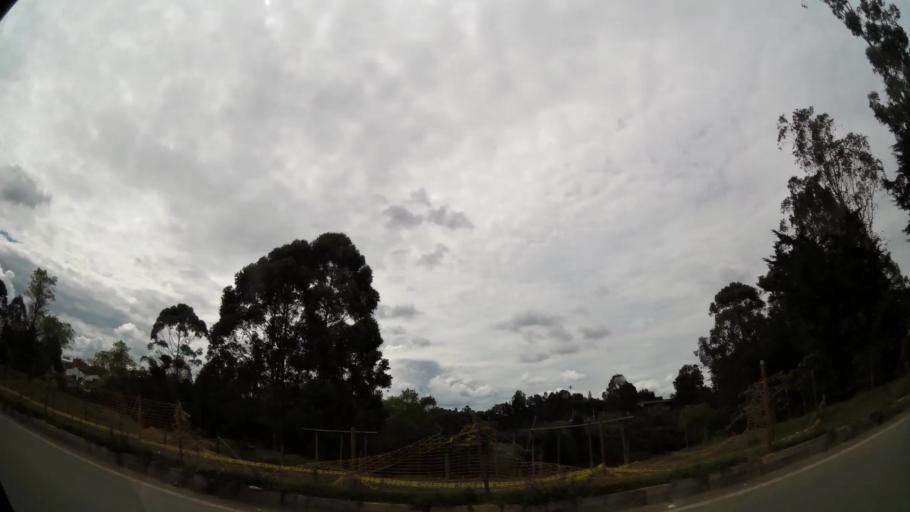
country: CO
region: Antioquia
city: Rionegro
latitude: 6.1606
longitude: -75.3656
